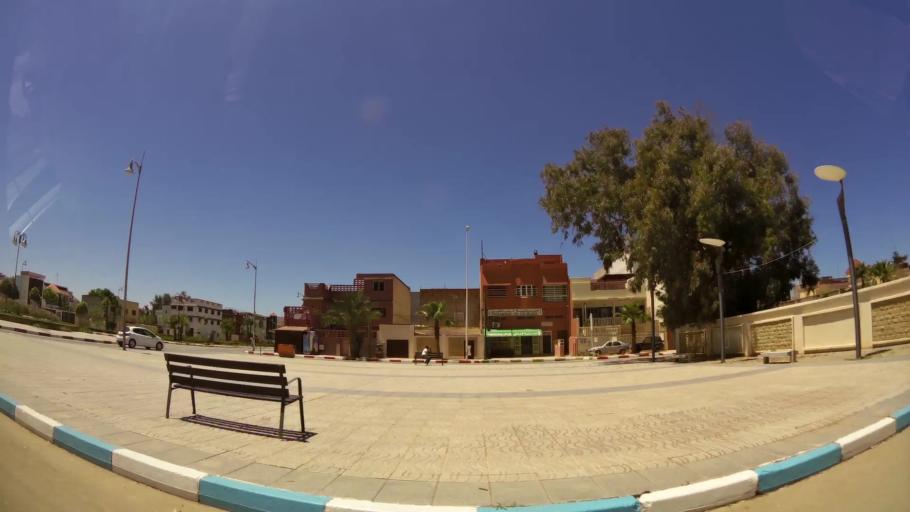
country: MA
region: Oriental
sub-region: Berkane-Taourirt
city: Madagh
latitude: 35.0835
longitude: -2.2203
